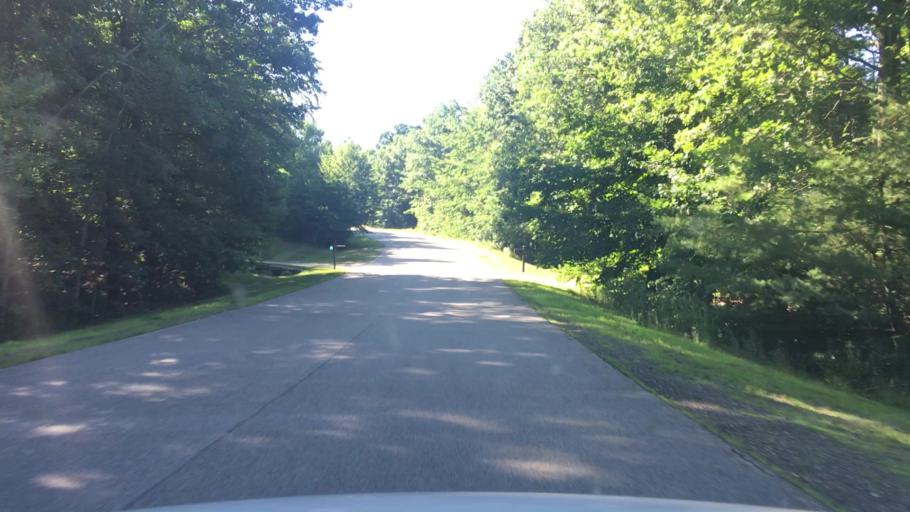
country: US
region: New Hampshire
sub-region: Rockingham County
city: Newmarket
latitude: 43.0353
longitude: -70.9586
